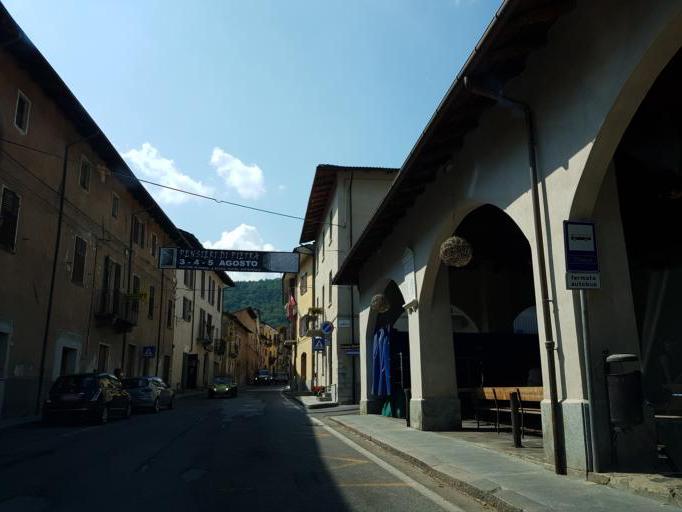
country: IT
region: Piedmont
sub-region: Provincia di Cuneo
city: San Damiano Macra
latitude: 44.4883
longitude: 7.2567
